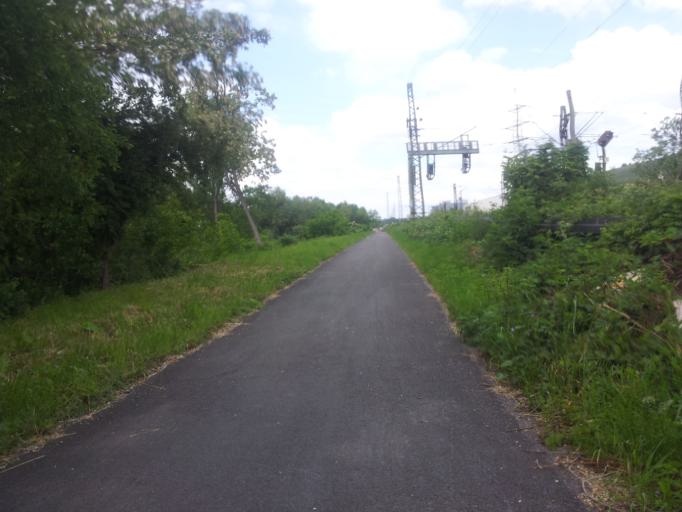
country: DE
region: Baden-Wuerttemberg
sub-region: Regierungsbezirk Stuttgart
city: Ostfildern
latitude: 48.7662
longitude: 9.2643
